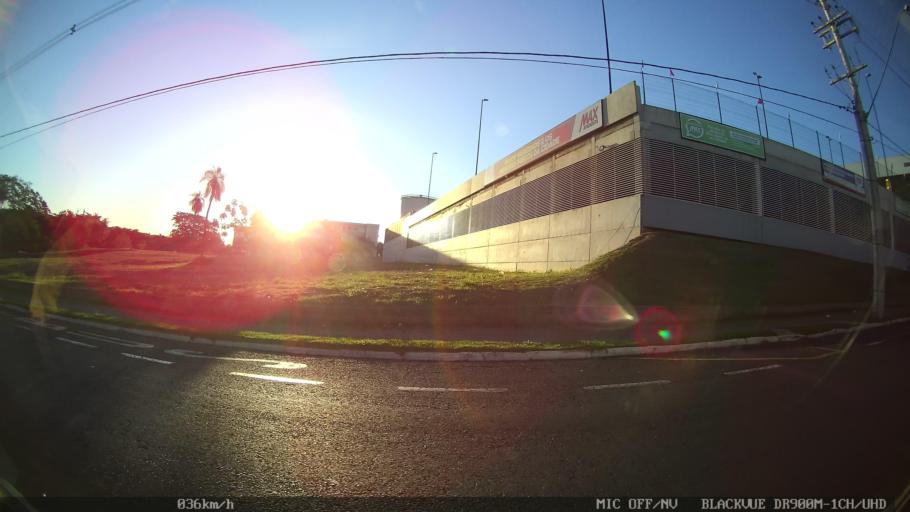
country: BR
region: Sao Paulo
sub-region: Sao Jose Do Rio Preto
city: Sao Jose do Rio Preto
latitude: -20.7817
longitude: -49.3790
